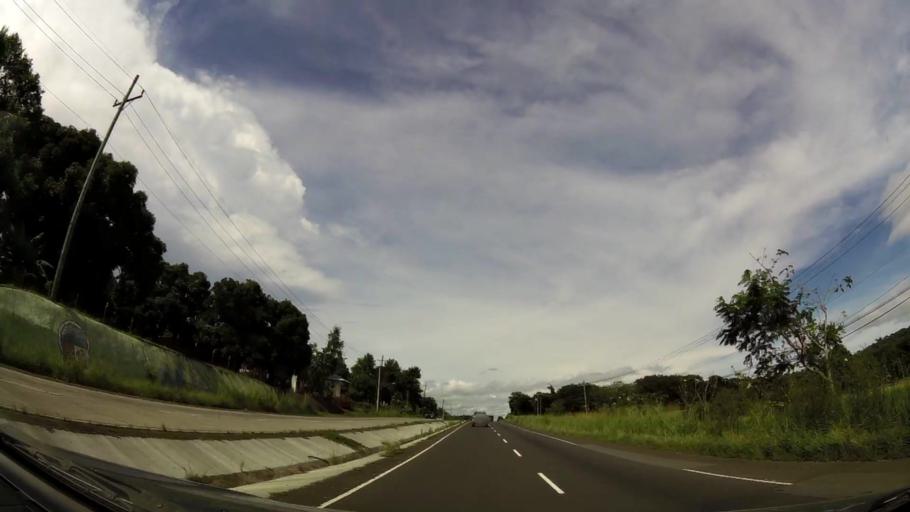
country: PA
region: Panama
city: Capira
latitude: 8.7273
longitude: -79.8850
